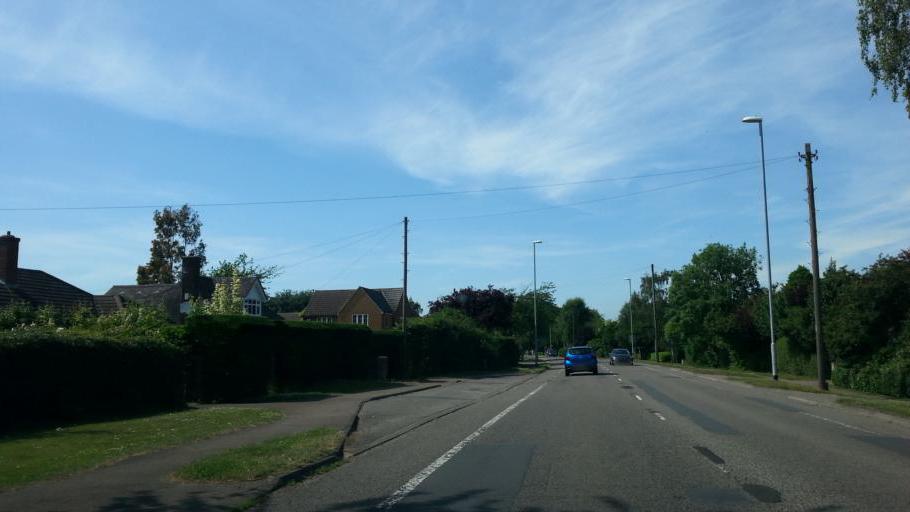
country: GB
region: England
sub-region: Cambridgeshire
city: Grantchester
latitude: 52.1639
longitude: 0.1215
